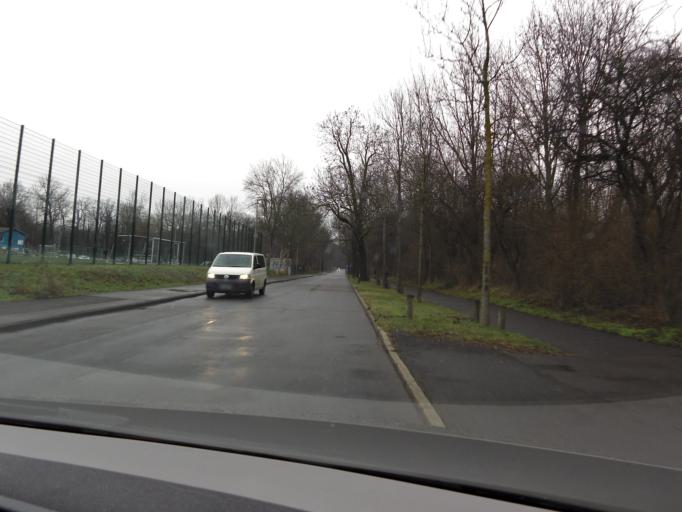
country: DE
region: Saxony
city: Leipzig
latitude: 51.3459
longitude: 12.3412
